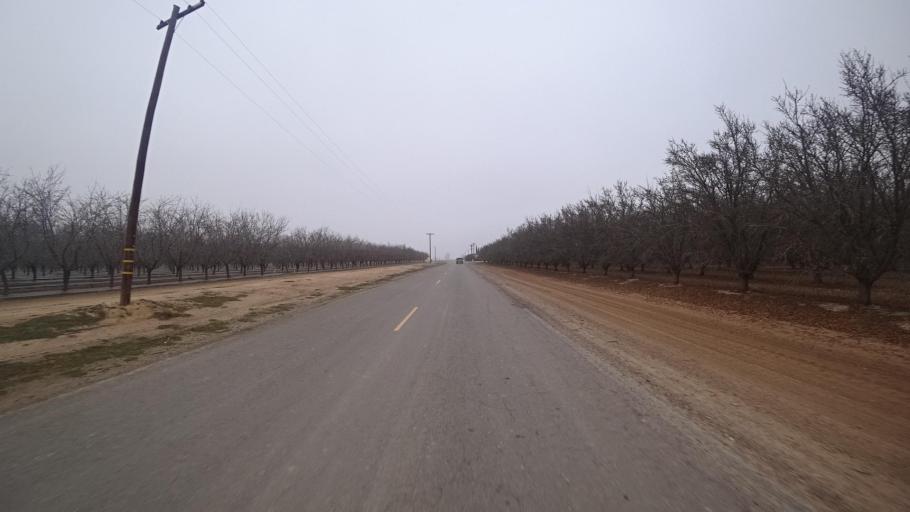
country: US
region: California
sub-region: Kern County
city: Lost Hills
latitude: 35.5847
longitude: -119.5271
